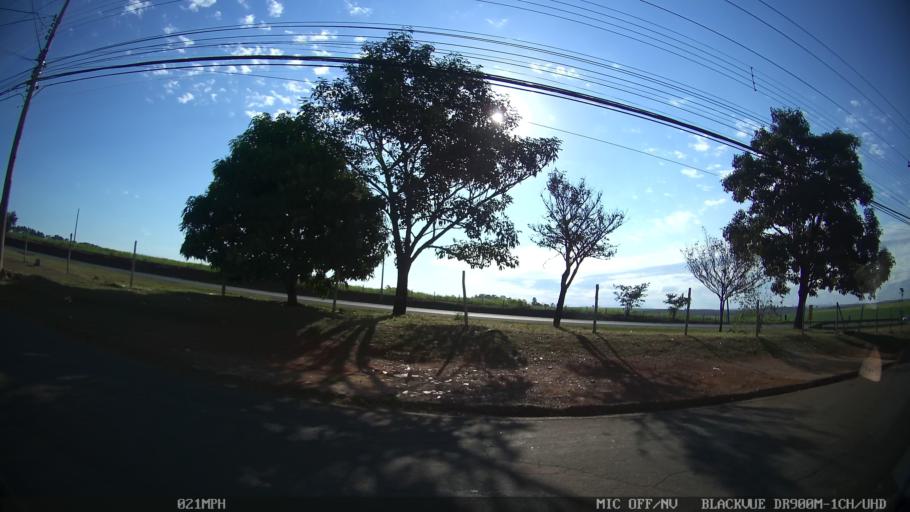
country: BR
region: Sao Paulo
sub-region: Piracicaba
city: Piracicaba
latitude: -22.6855
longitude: -47.6387
